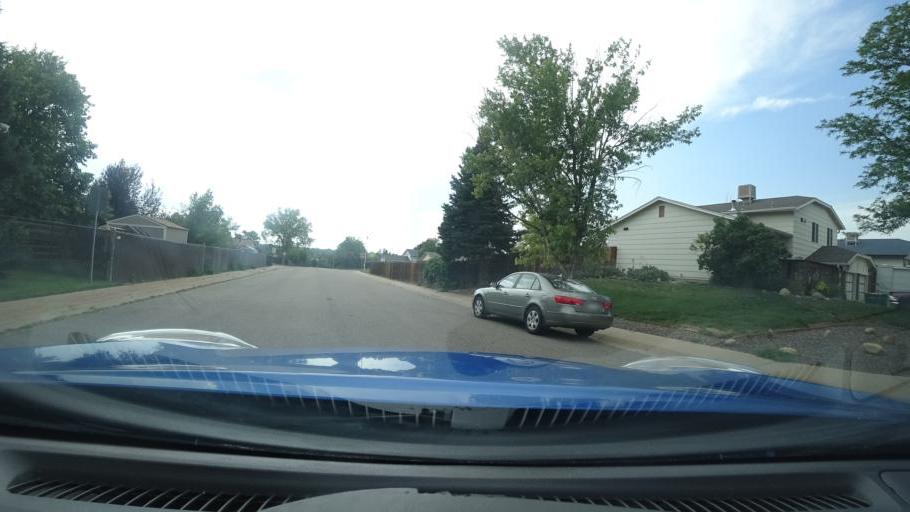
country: US
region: Colorado
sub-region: Adams County
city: Aurora
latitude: 39.6873
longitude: -104.7952
